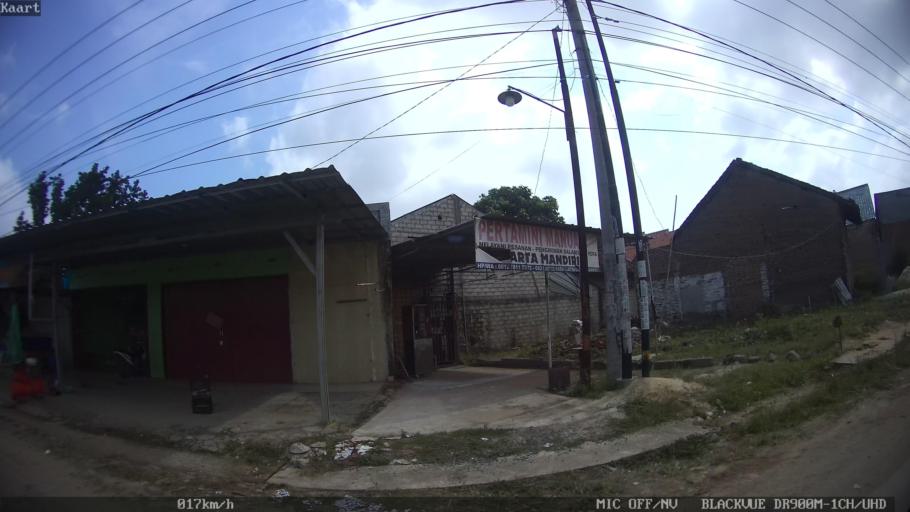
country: ID
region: Lampung
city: Kedaton
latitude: -5.3302
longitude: 105.2907
